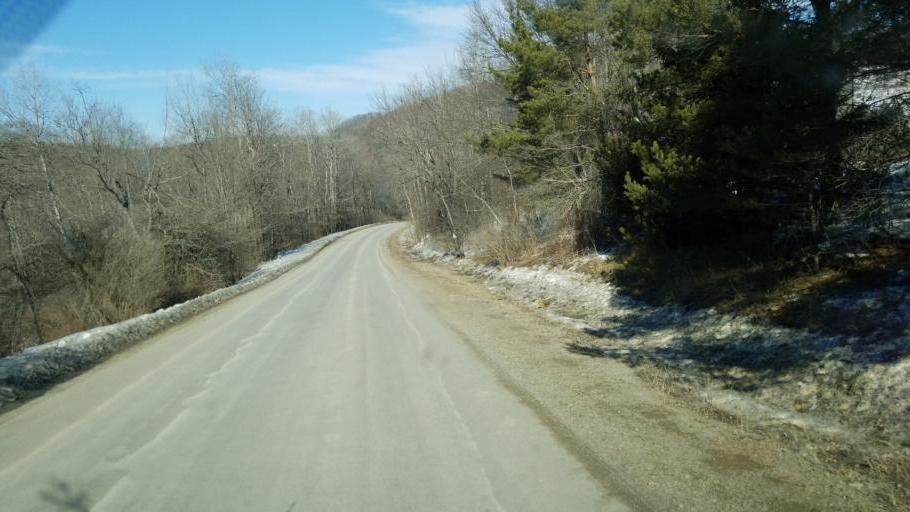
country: US
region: New York
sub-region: Allegany County
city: Andover
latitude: 42.1488
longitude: -77.7707
